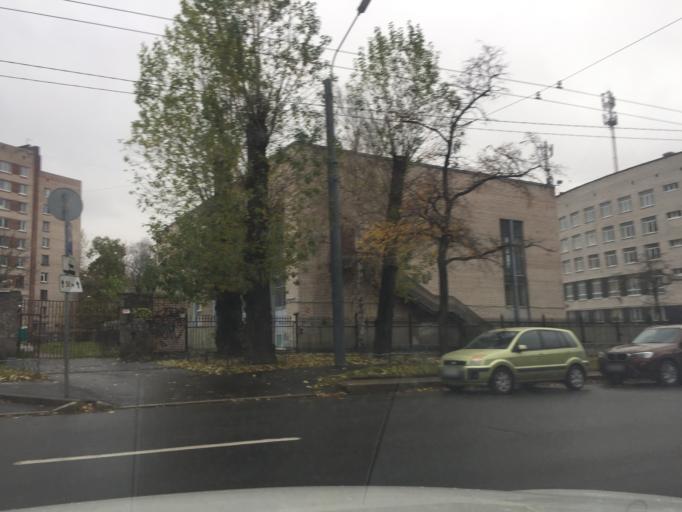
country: RU
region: Leningrad
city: Svetlanovskiy
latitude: 60.0045
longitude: 30.3307
